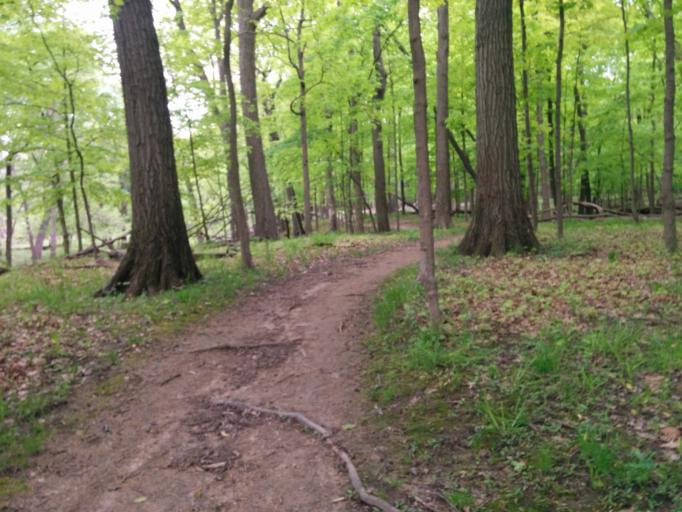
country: US
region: Illinois
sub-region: Cook County
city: Franklin Park
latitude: 41.9474
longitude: -87.8534
